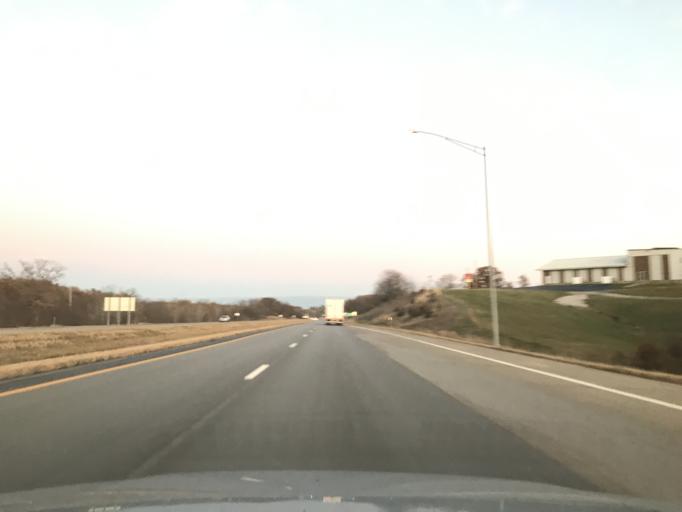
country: US
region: Missouri
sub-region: Marion County
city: Hannibal
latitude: 39.7142
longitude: -91.4137
